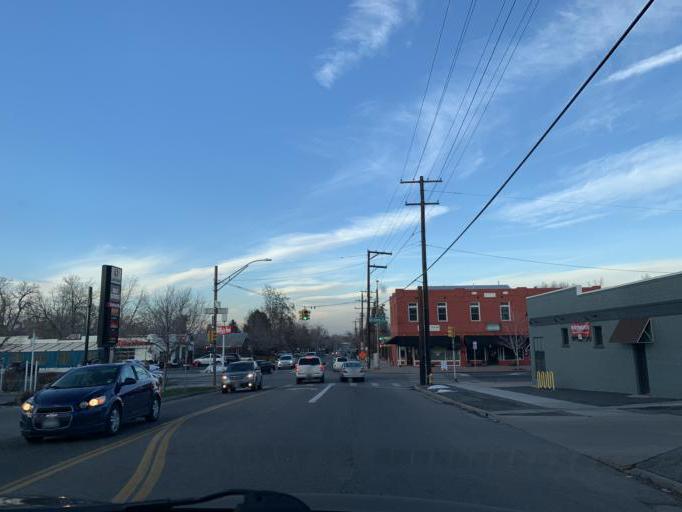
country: US
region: Colorado
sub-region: Adams County
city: Berkley
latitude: 39.7763
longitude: -105.0346
